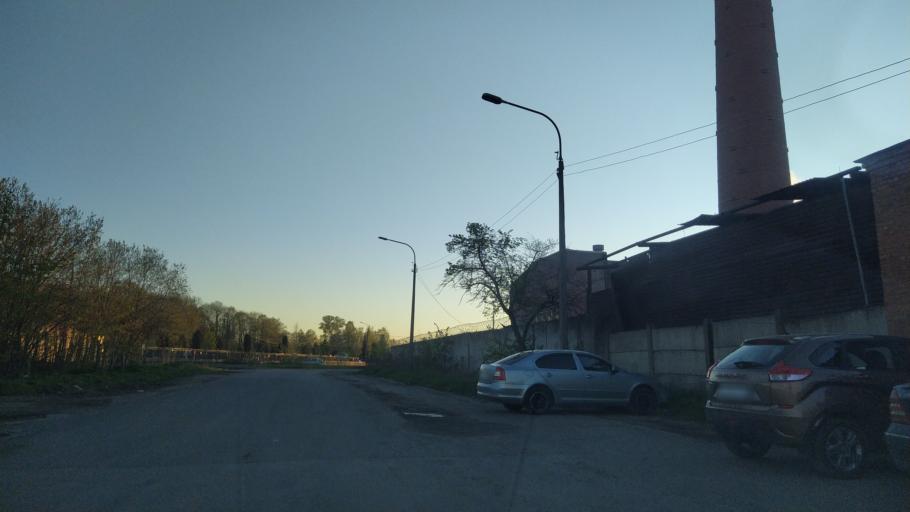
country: RU
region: St.-Petersburg
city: Pushkin
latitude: 59.6950
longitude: 30.3919
